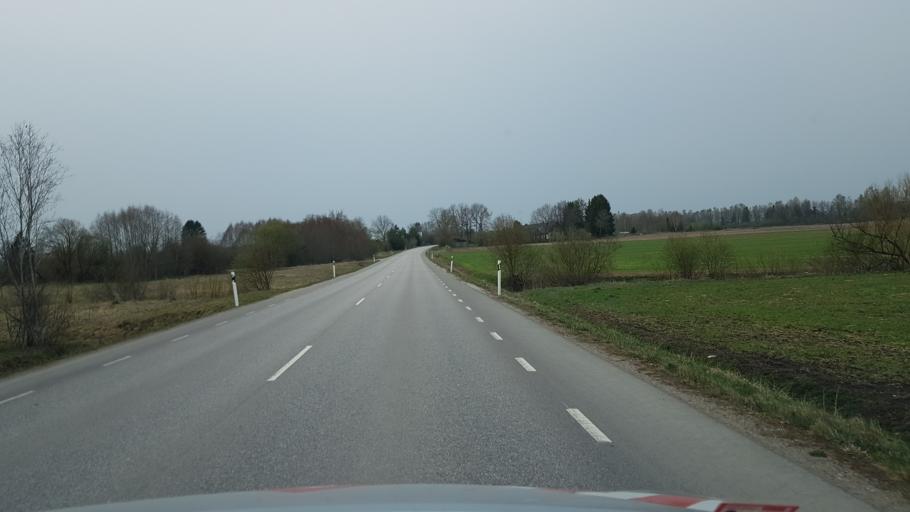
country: EE
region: Harju
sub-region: Raasiku vald
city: Arukula
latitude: 59.3772
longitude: 25.0138
